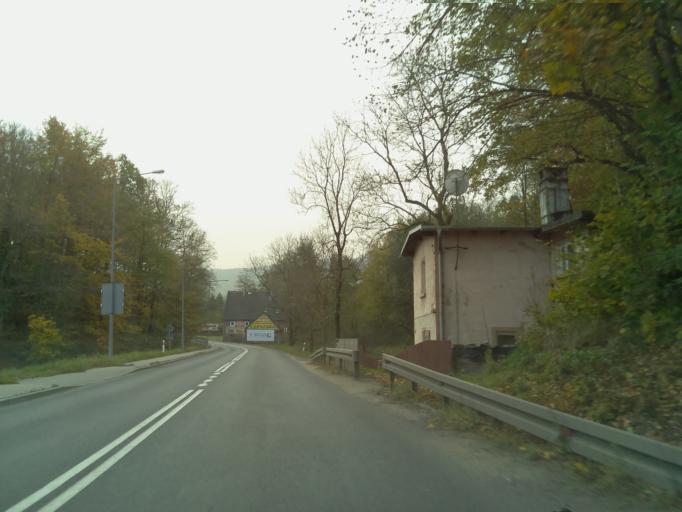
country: PL
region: Lower Silesian Voivodeship
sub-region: Powiat jeleniogorski
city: Janowice Wielkie
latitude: 50.9136
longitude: 15.9577
